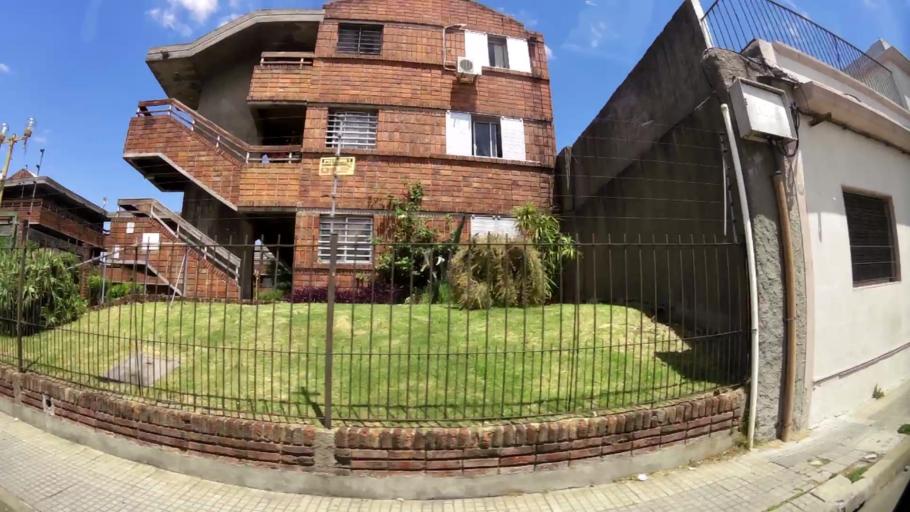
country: UY
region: Montevideo
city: Montevideo
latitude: -34.8692
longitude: -56.1935
